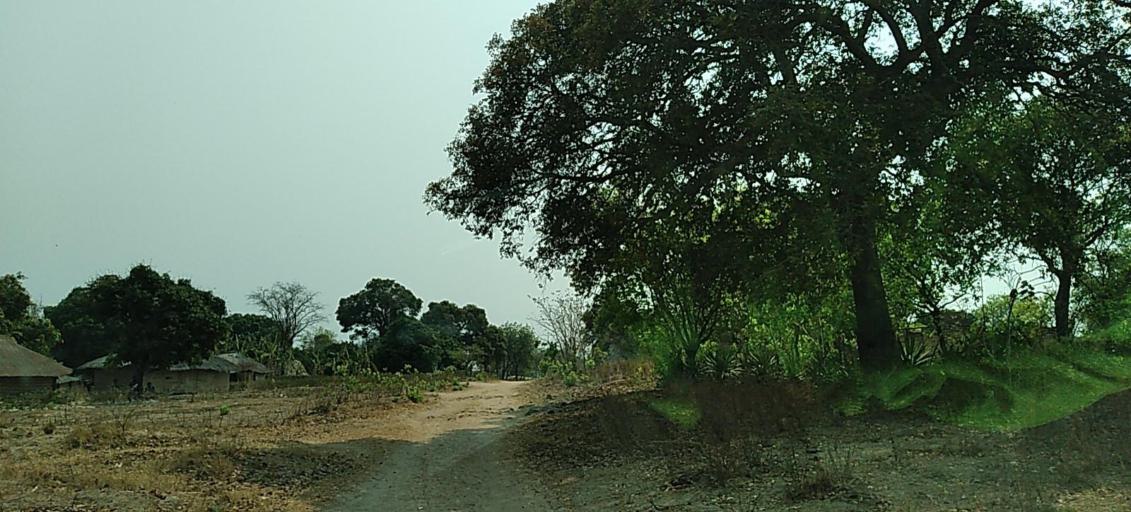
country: ZM
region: North-Western
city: Zambezi
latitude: -13.0578
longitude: 23.4837
